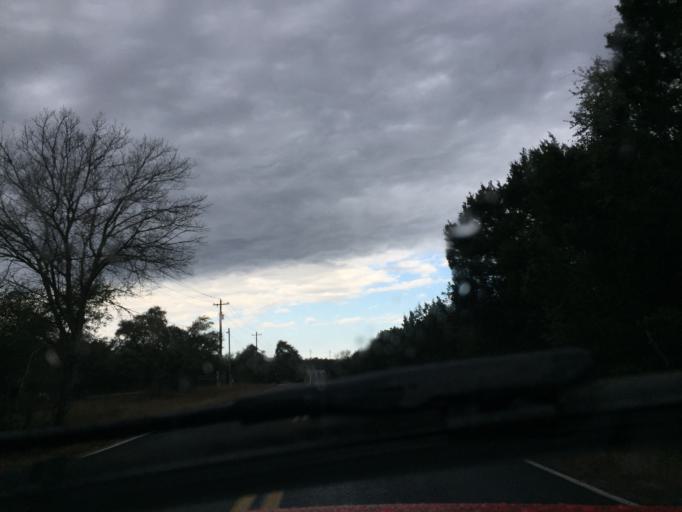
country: US
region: Texas
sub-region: Williamson County
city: Leander
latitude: 30.6015
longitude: -97.9326
